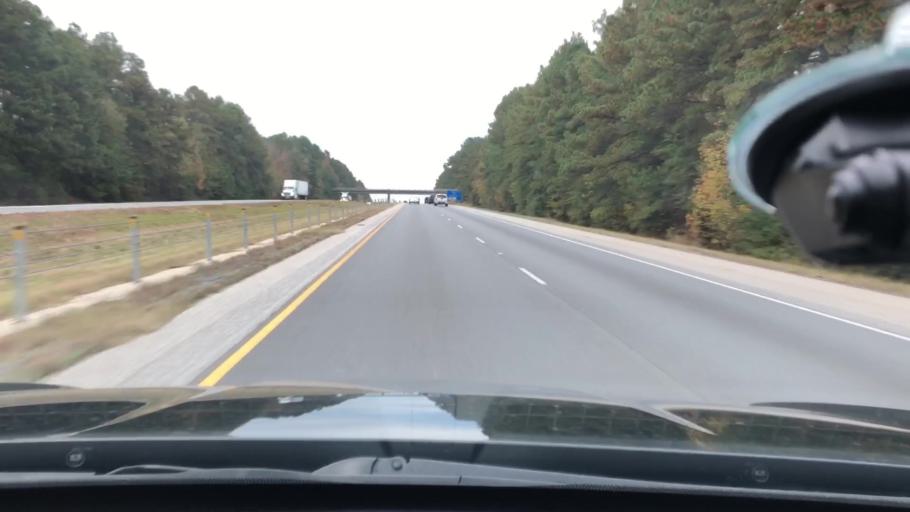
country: US
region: Arkansas
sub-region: Clark County
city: Arkadelphia
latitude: 34.0897
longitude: -93.1098
